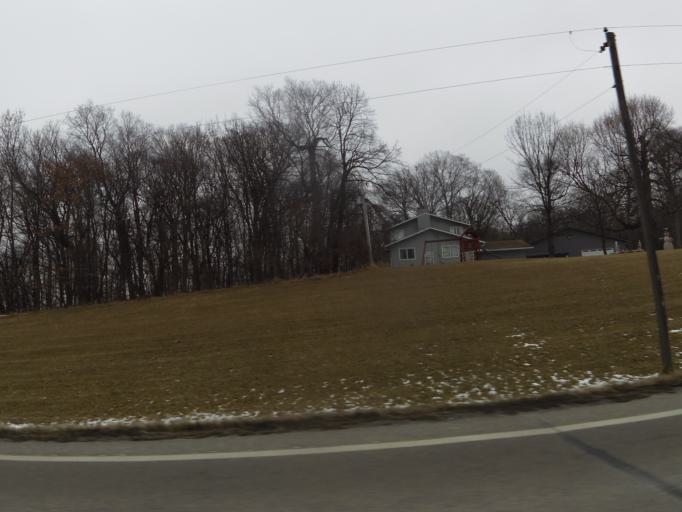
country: US
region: Minnesota
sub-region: Carver County
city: Watertown
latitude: 44.9976
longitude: -93.8488
